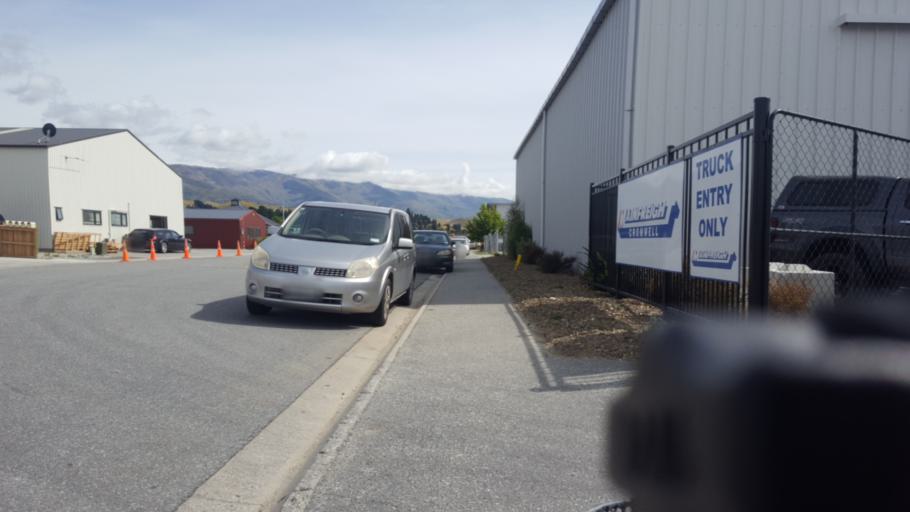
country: NZ
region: Otago
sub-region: Queenstown-Lakes District
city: Wanaka
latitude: -45.0510
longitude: 169.1894
